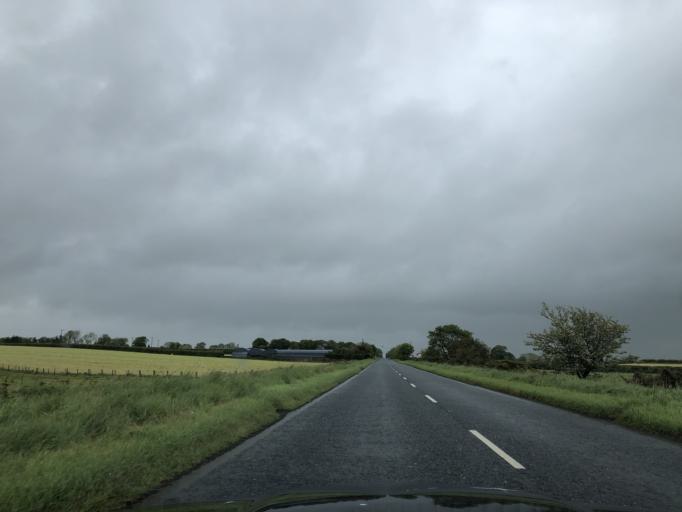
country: GB
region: Northern Ireland
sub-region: Moyle District
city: Ballycastle
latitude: 55.1741
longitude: -6.3386
